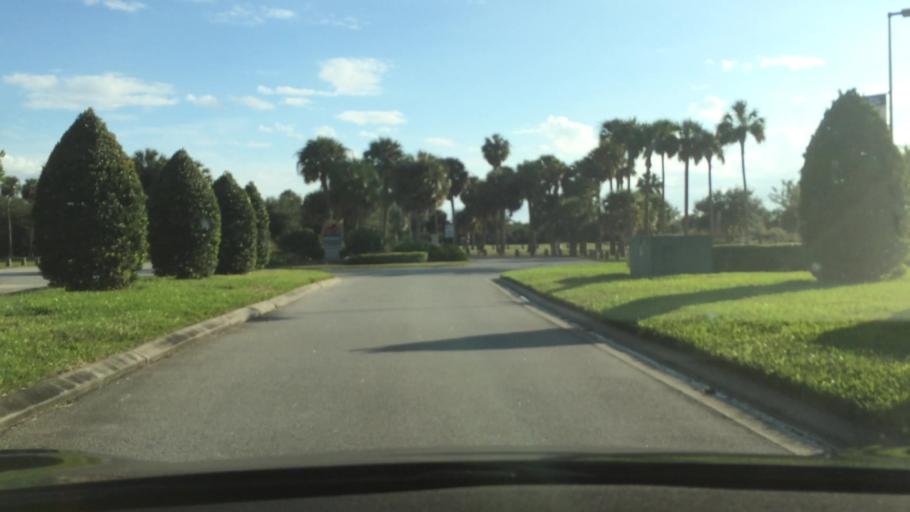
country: US
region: Florida
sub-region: Hillsborough County
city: Town 'n' Country
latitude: 27.9515
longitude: -82.5425
